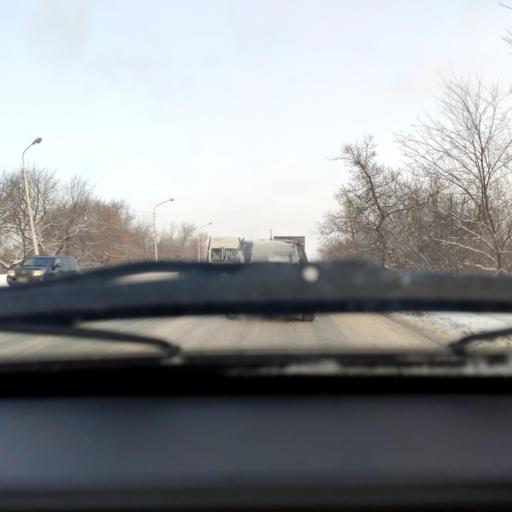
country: RU
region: Bashkortostan
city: Ufa
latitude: 54.8073
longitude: 56.0863
